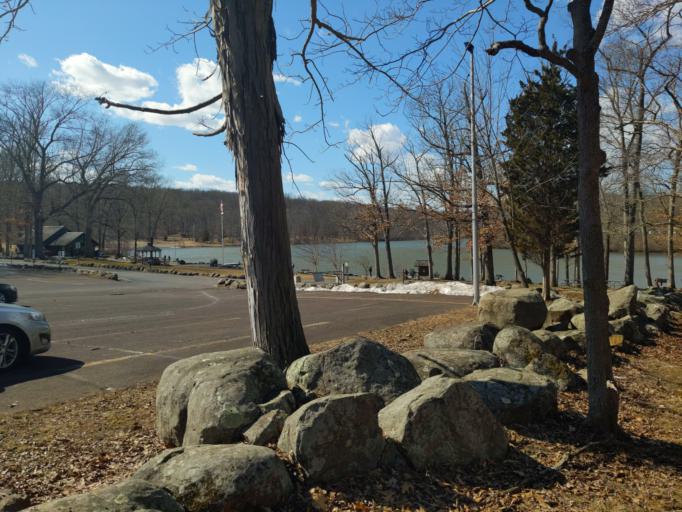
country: US
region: Pennsylvania
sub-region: Montgomery County
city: Woxall
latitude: 40.3323
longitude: -75.4831
